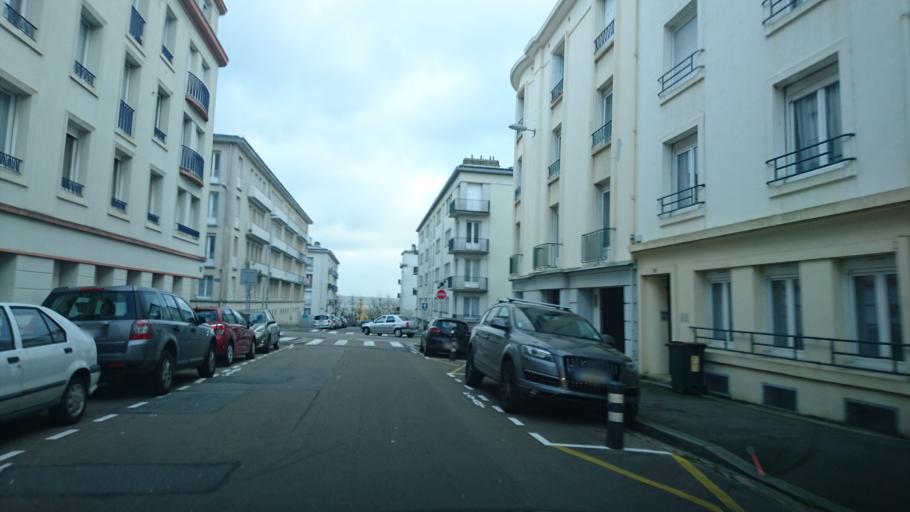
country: FR
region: Brittany
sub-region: Departement du Finistere
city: Brest
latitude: 48.3850
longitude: -4.4876
